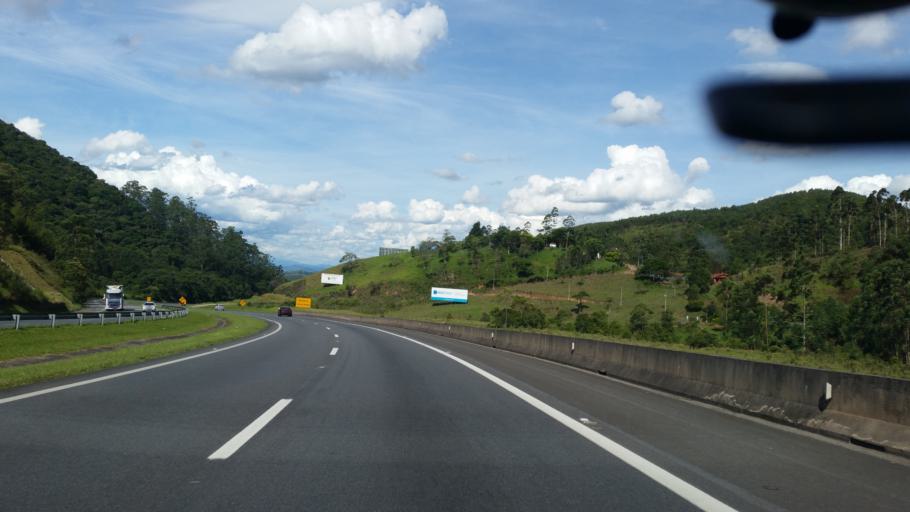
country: BR
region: Sao Paulo
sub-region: Santa Isabel
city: Santa Isabel
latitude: -23.1755
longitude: -46.2526
